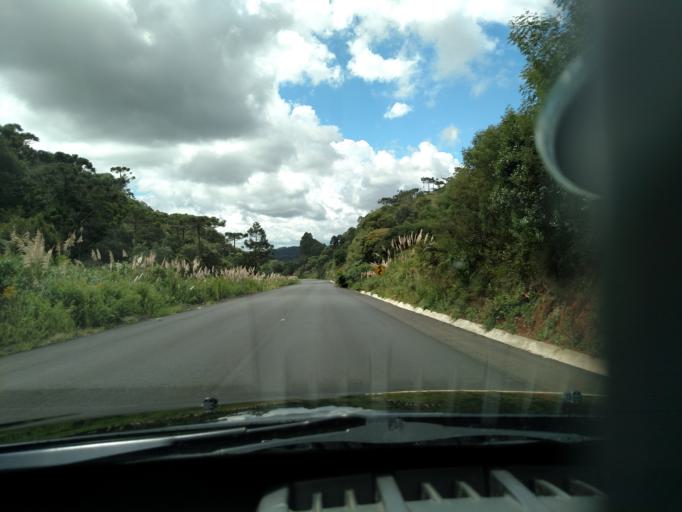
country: BR
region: Santa Catarina
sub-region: Lages
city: Lages
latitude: -27.9626
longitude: -50.0981
